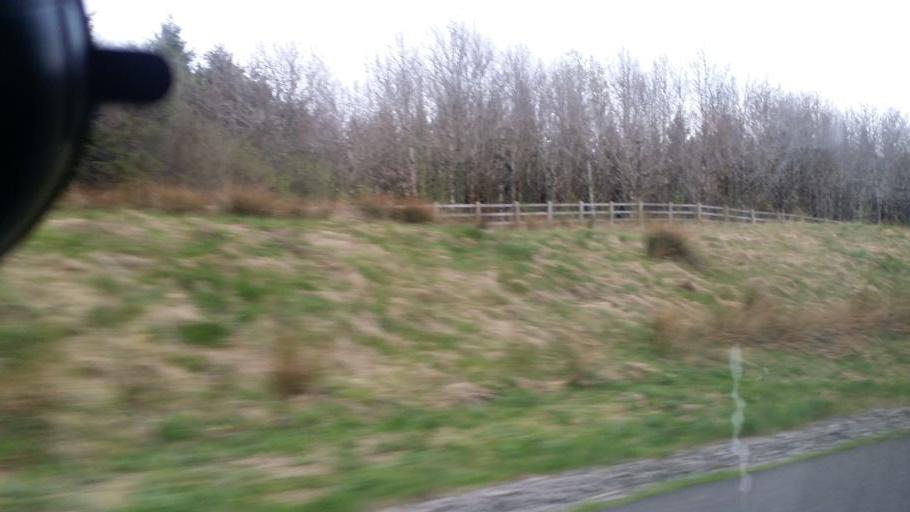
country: IE
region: Ulster
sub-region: An Cabhan
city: Belturbet
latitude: 54.0865
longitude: -7.4459
